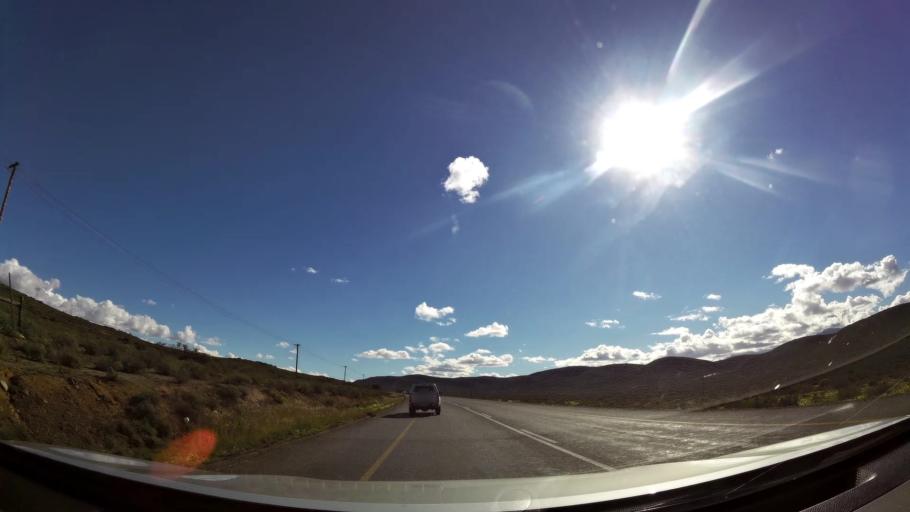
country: ZA
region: Western Cape
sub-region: Cape Winelands District Municipality
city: Worcester
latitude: -33.7394
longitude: 19.6900
